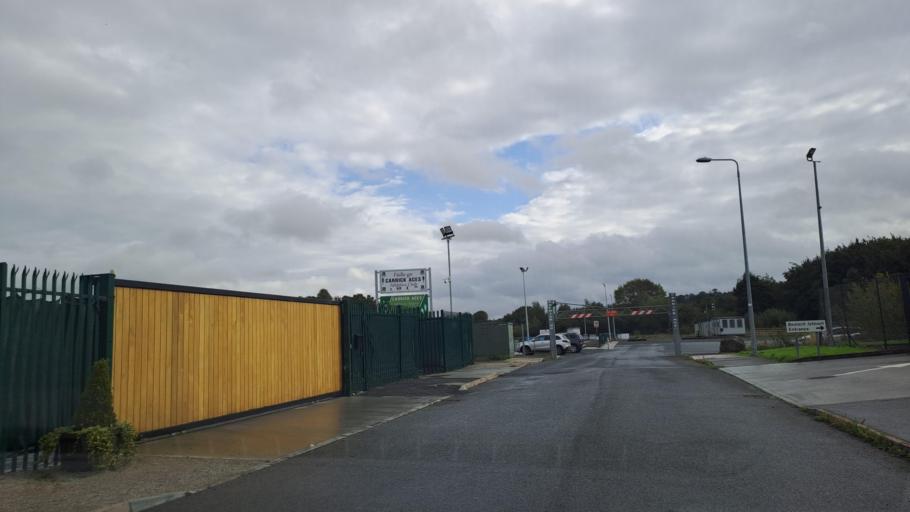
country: IE
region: Ulster
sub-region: County Monaghan
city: Carrickmacross
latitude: 53.9675
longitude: -6.7080
